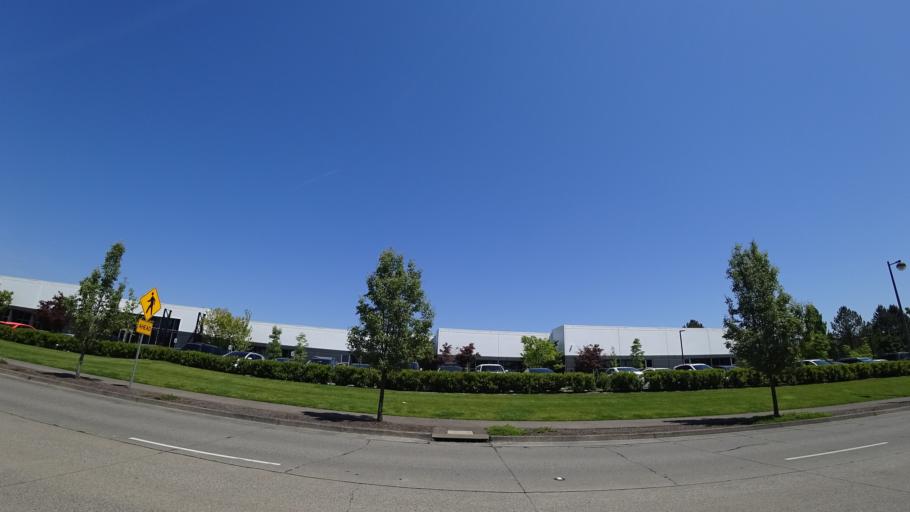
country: US
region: Oregon
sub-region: Washington County
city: Aloha
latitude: 45.4967
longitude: -122.8351
